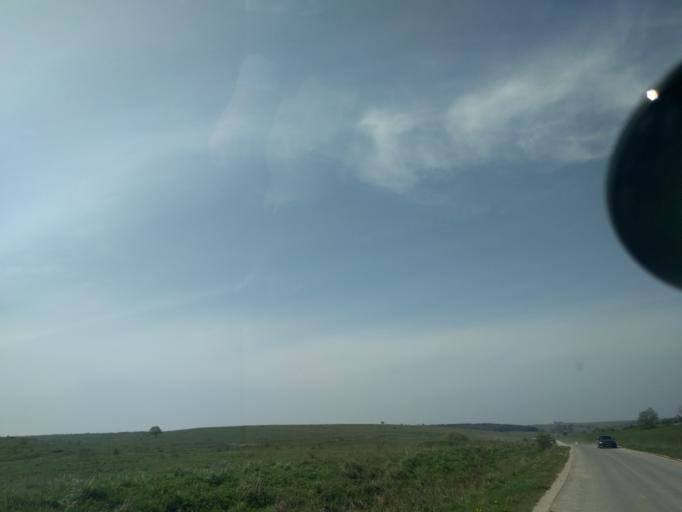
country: GB
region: England
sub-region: Wiltshire
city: Erlestoke
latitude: 51.2369
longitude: -2.0719
